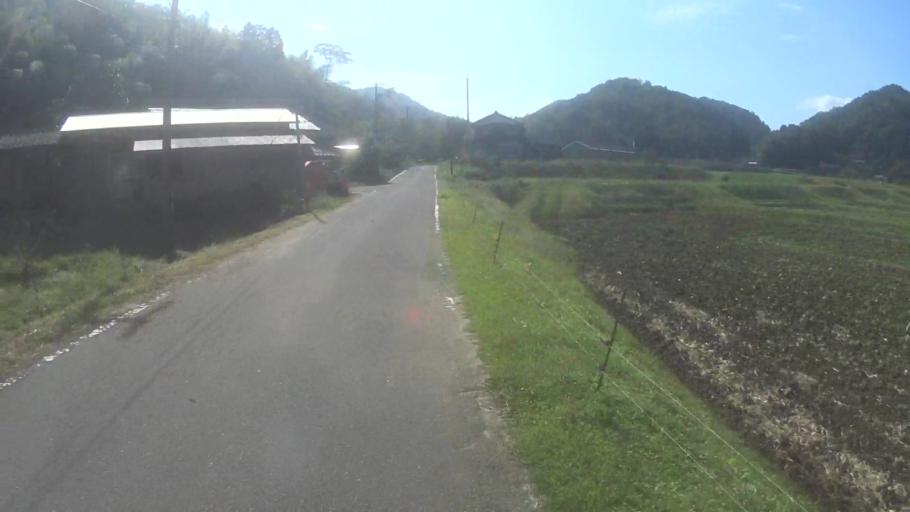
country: JP
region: Kyoto
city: Miyazu
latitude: 35.6940
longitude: 135.1516
